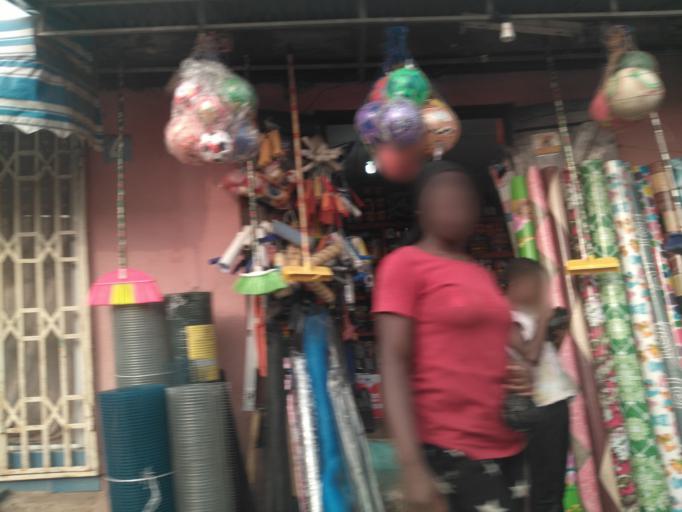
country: GH
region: Ashanti
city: Kumasi
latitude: 6.6776
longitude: -1.5921
